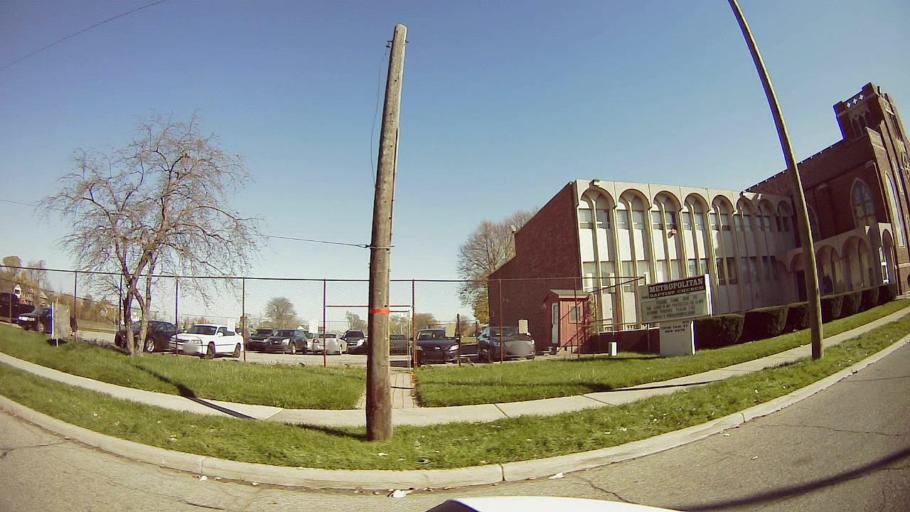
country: US
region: Michigan
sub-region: Wayne County
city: Highland Park
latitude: 42.3936
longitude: -83.1149
